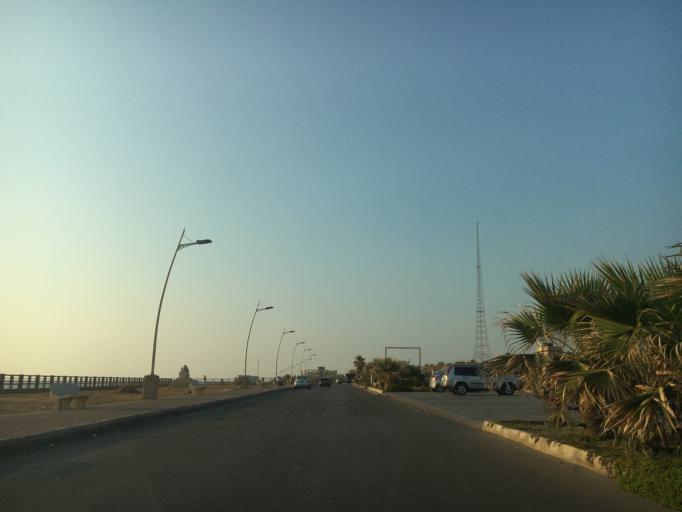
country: LB
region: Mont-Liban
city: Jbail
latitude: 34.1443
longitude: 35.6277
